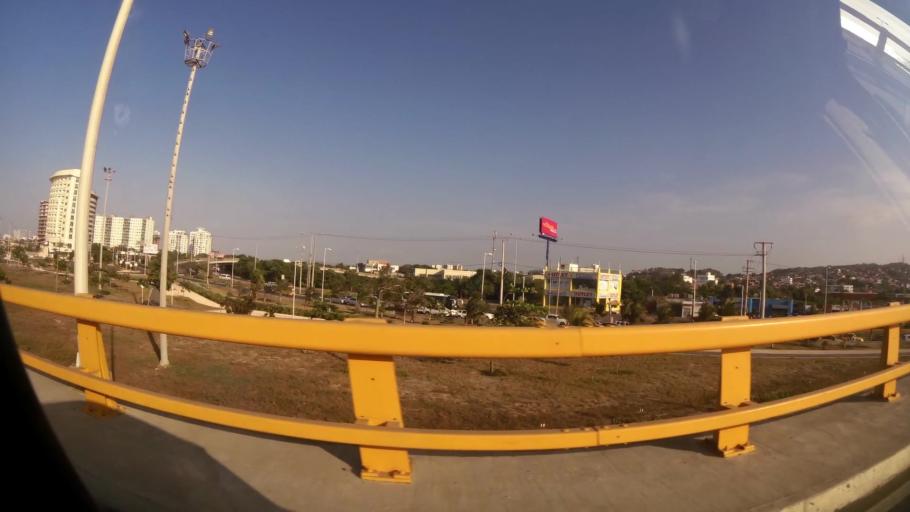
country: CO
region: Bolivar
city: Cartagena
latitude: 10.4420
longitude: -75.5278
